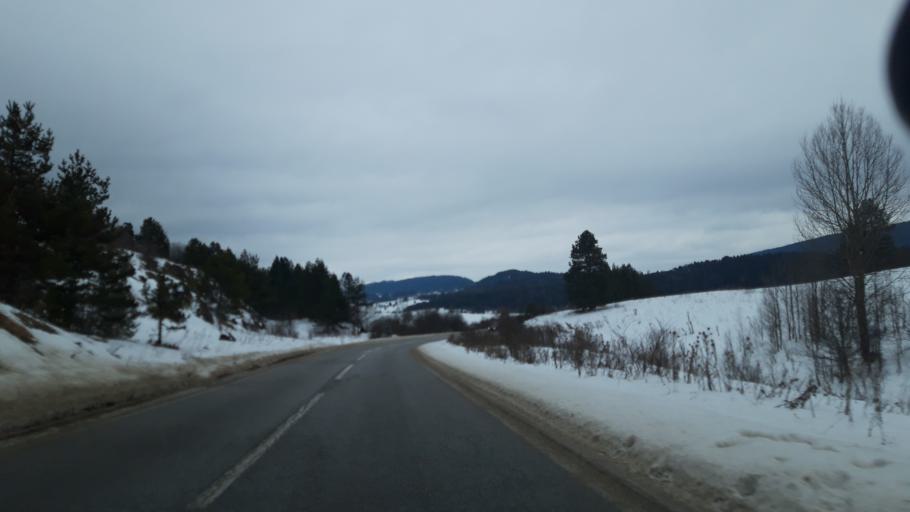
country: BA
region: Republika Srpska
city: Han Pijesak
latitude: 44.0101
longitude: 18.8893
